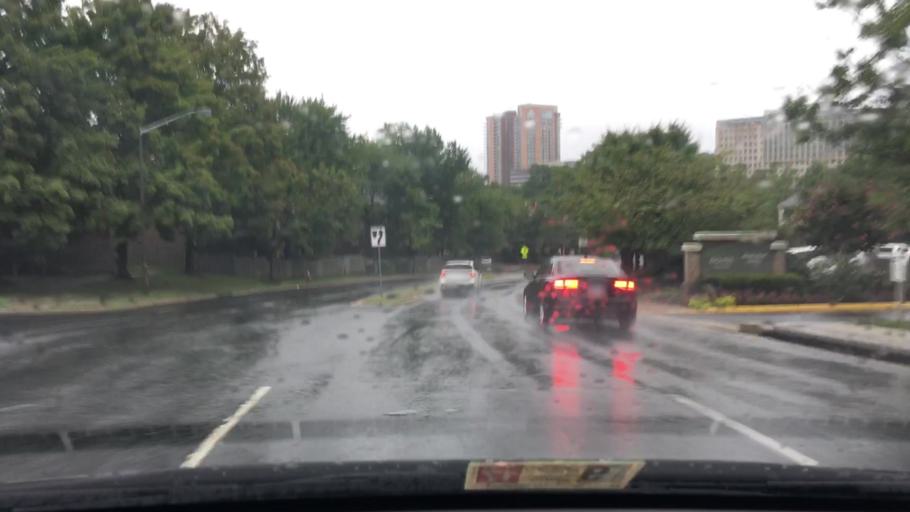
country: US
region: Virginia
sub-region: Fairfax County
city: Tysons Corner
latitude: 38.9205
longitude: -77.2388
